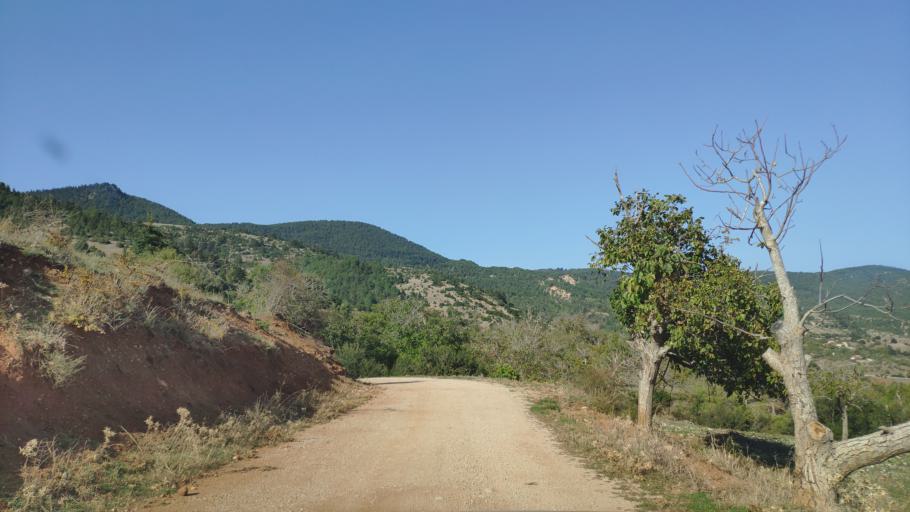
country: GR
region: West Greece
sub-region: Nomos Achaias
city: Aiyira
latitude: 37.9891
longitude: 22.3481
